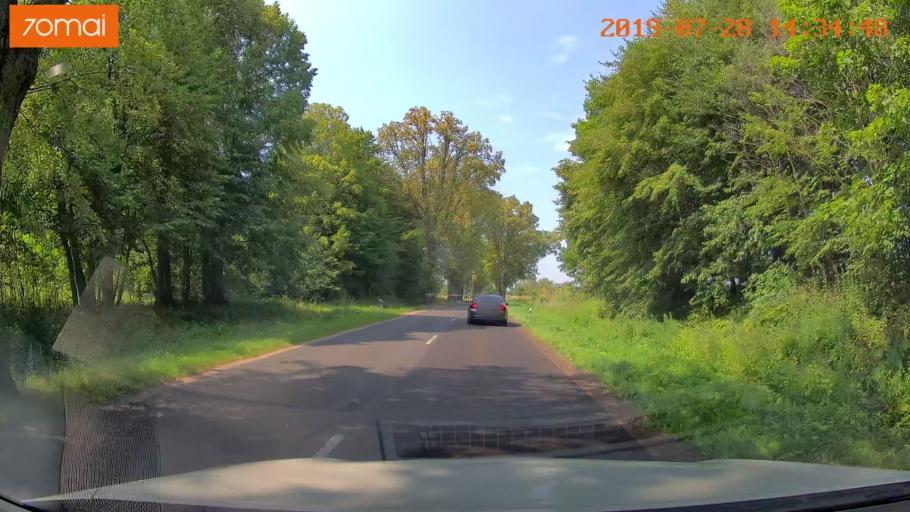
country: RU
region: Kaliningrad
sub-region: Gorod Kaliningrad
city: Yantarnyy
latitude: 54.8273
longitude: 20.0144
